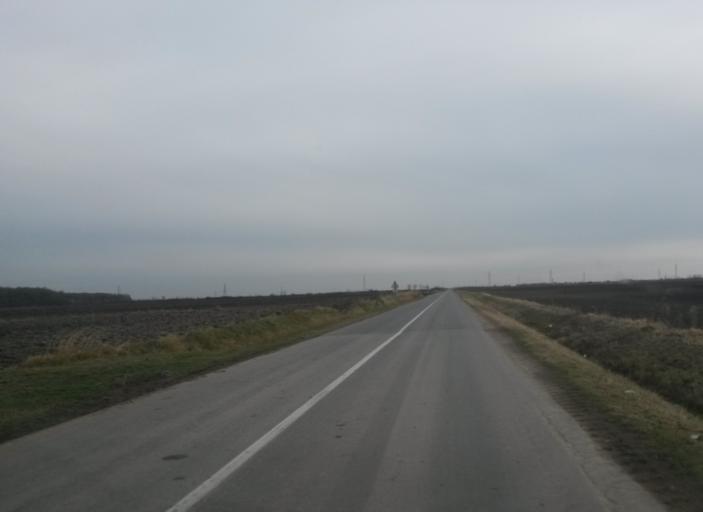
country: HR
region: Osjecko-Baranjska
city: Ovcara
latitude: 45.5023
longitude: 18.5992
